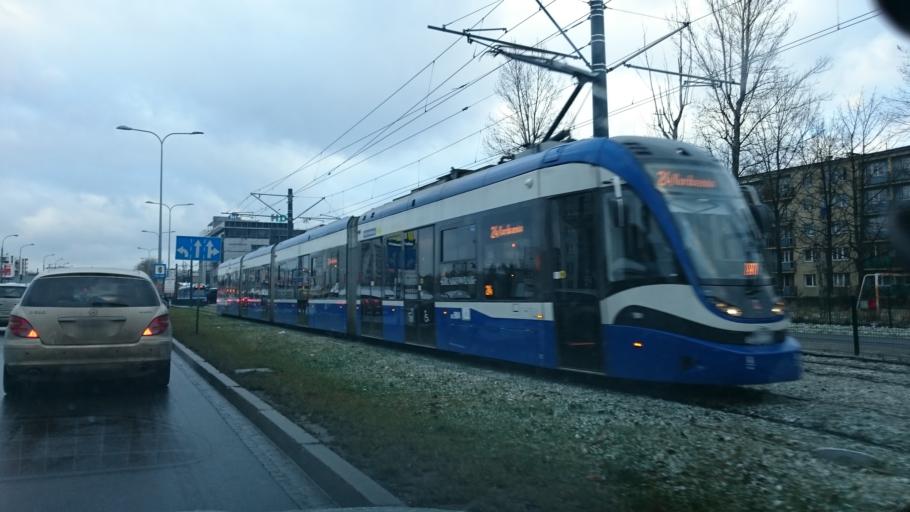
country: PL
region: Lesser Poland Voivodeship
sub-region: Krakow
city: Krakow
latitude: 50.0317
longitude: 19.9719
